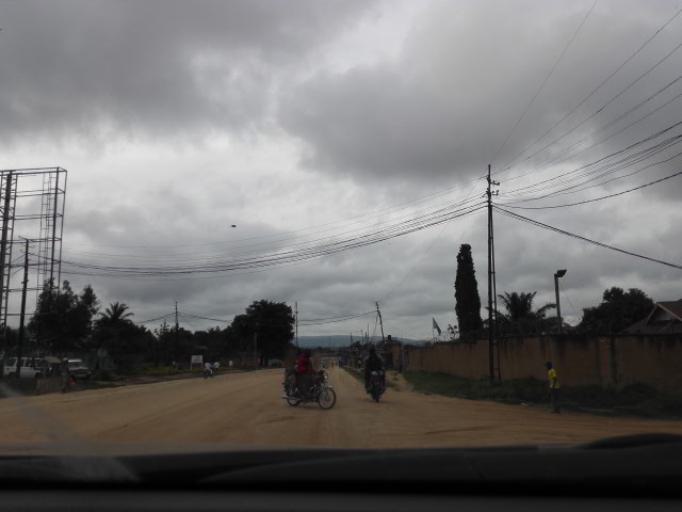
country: CD
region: Eastern Province
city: Bunia
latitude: 1.5478
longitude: 30.2492
